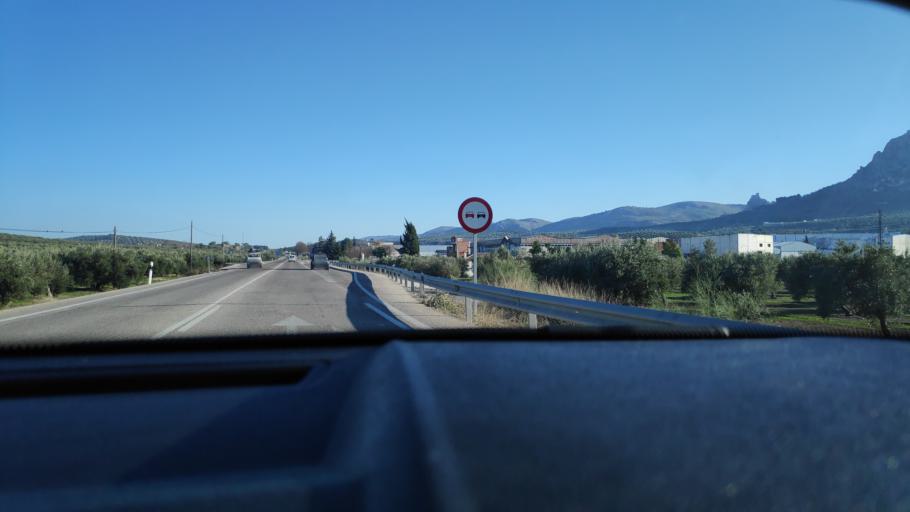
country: ES
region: Andalusia
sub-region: Province of Cordoba
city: Luque
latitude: 37.5827
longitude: -4.2868
